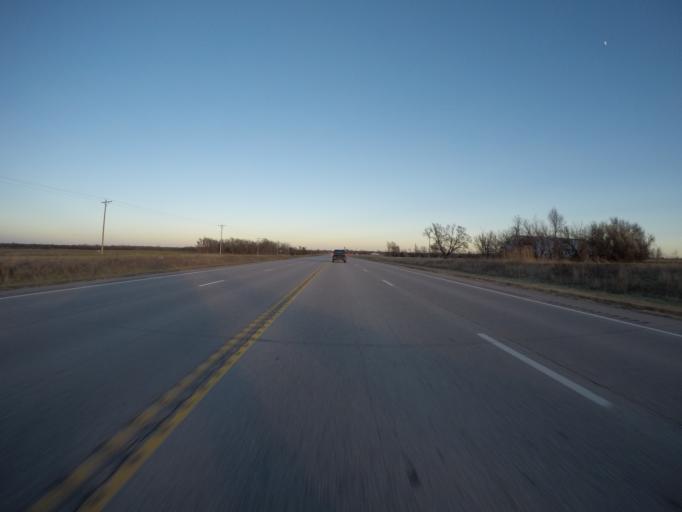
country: US
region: Kansas
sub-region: Marion County
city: Peabody
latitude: 38.1746
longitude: -97.1400
